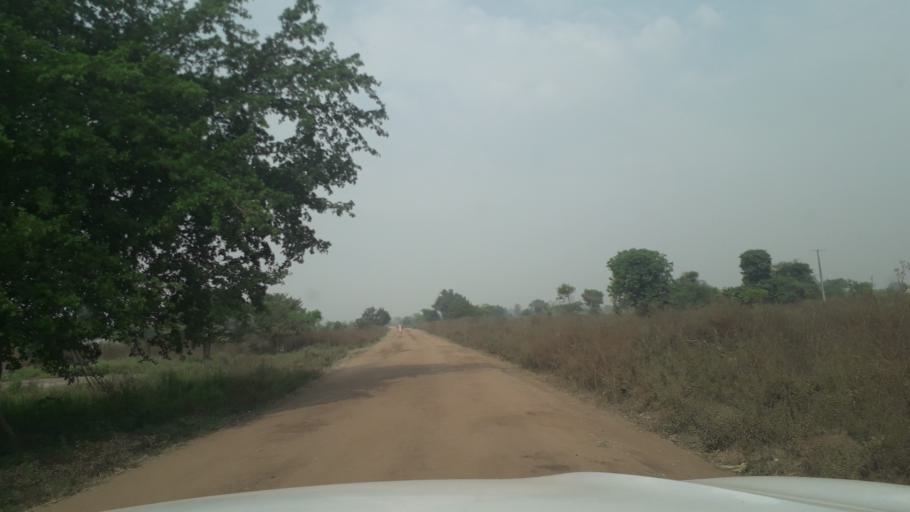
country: ET
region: Gambela
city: Gambela
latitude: 8.3286
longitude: 33.7355
